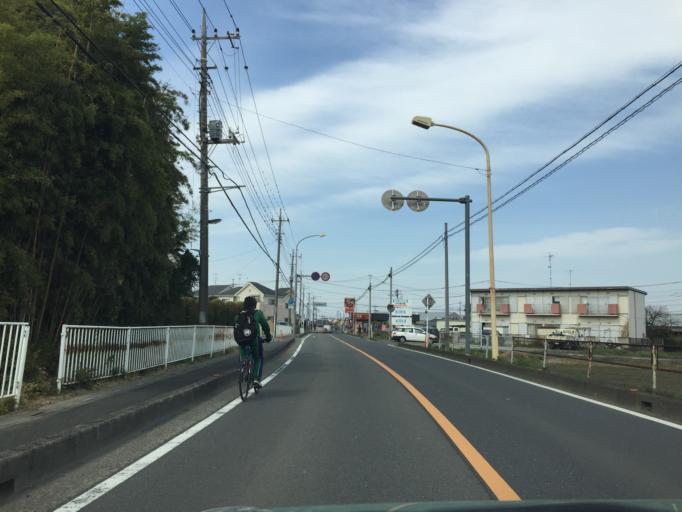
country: JP
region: Saitama
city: Yono
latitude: 35.8740
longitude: 139.5988
